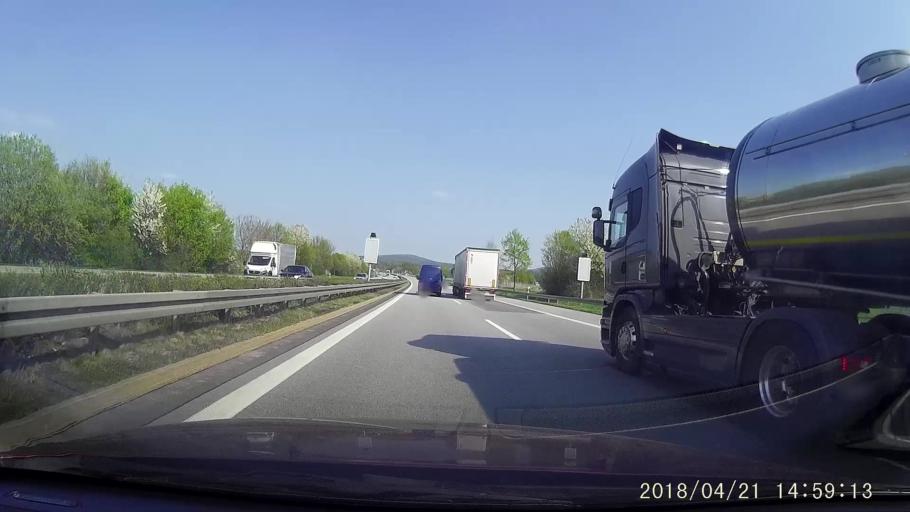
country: DE
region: Saxony
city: Reichenbach
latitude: 51.2039
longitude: 14.7530
